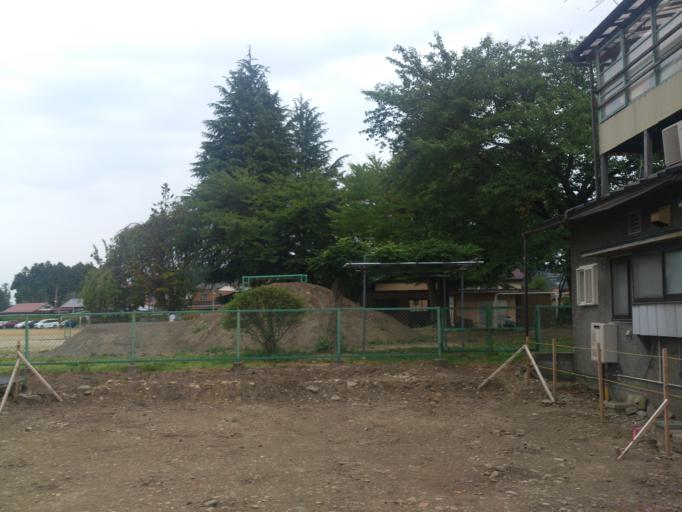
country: JP
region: Iwate
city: Ichinoseki
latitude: 38.9293
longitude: 141.1205
